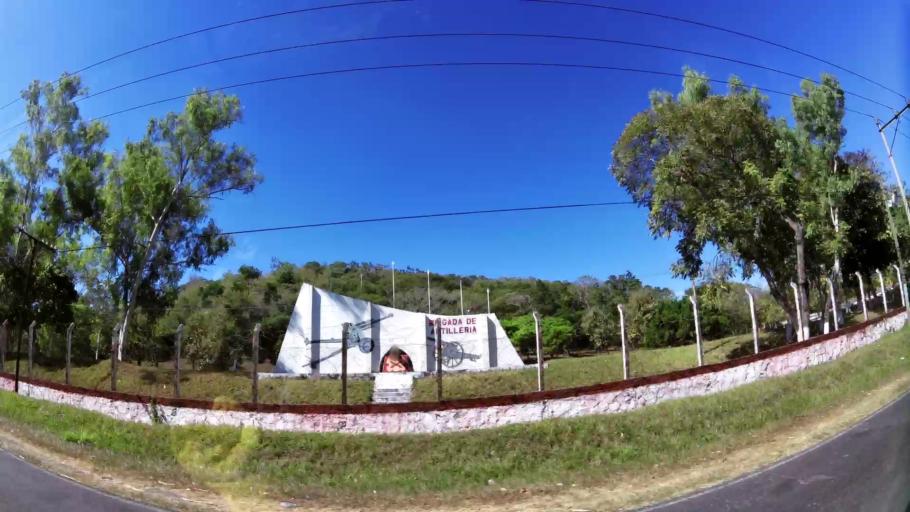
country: SV
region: La Libertad
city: San Juan Opico
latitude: 13.8388
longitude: -89.3599
